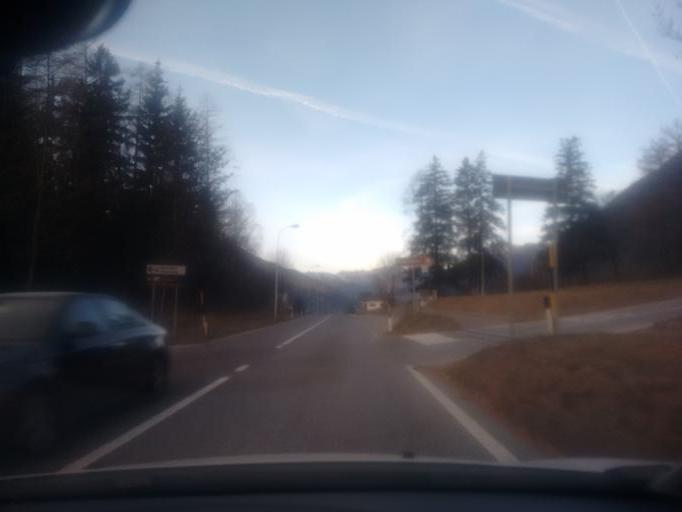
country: IT
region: Trentino-Alto Adige
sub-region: Bolzano
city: Campo di Trens
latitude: 46.8714
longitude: 11.4875
